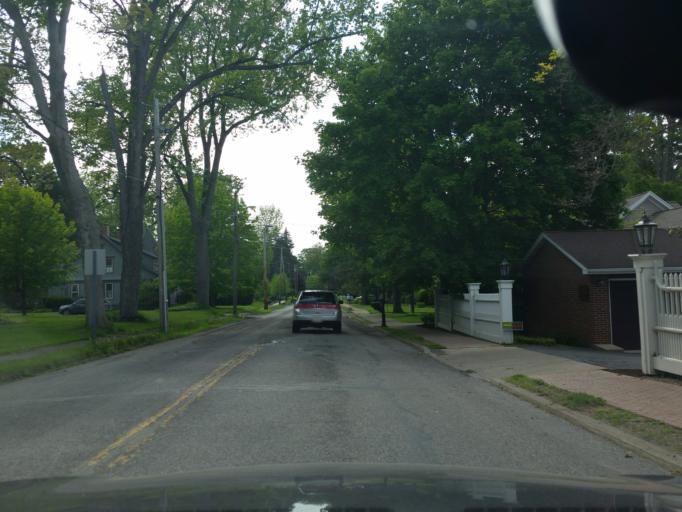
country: US
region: New York
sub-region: Chautauqua County
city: Lakewood
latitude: 42.1057
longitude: -79.3281
